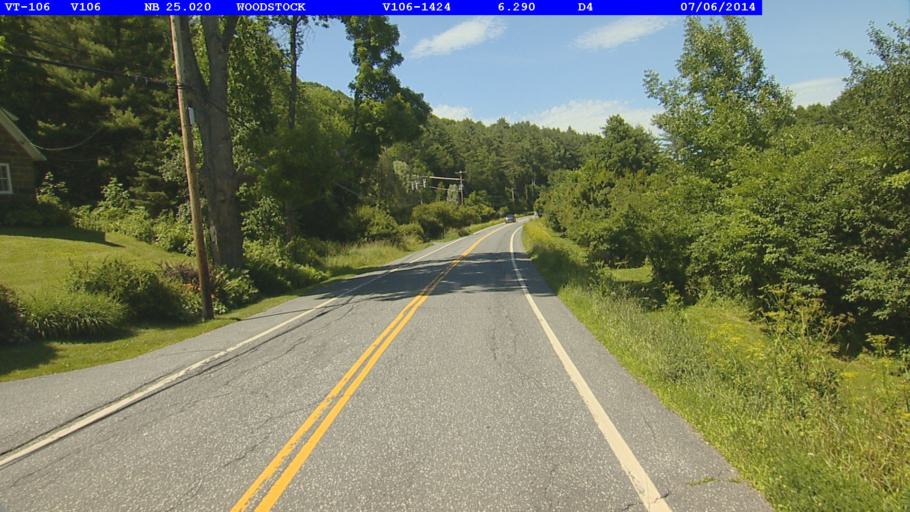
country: US
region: Vermont
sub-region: Windsor County
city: Woodstock
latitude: 43.6108
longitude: -72.5169
